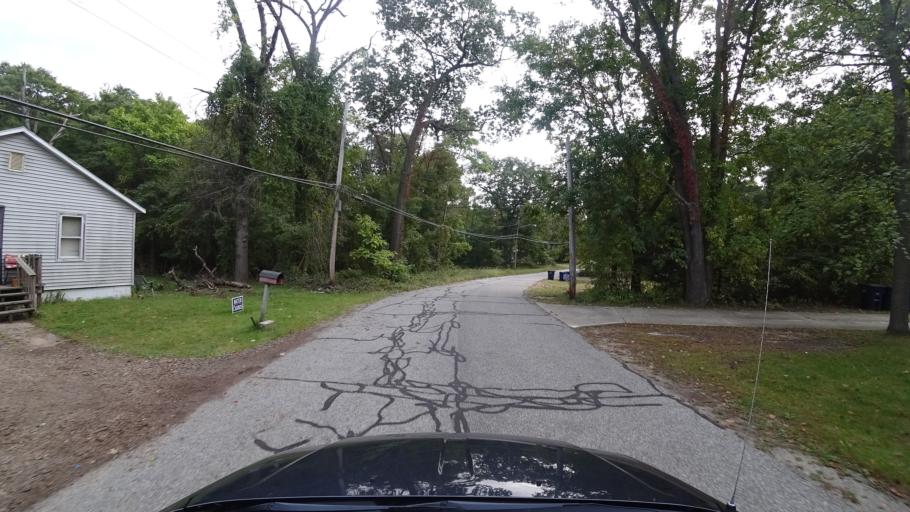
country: US
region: Indiana
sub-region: LaPorte County
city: Long Beach
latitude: 41.7297
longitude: -86.8597
